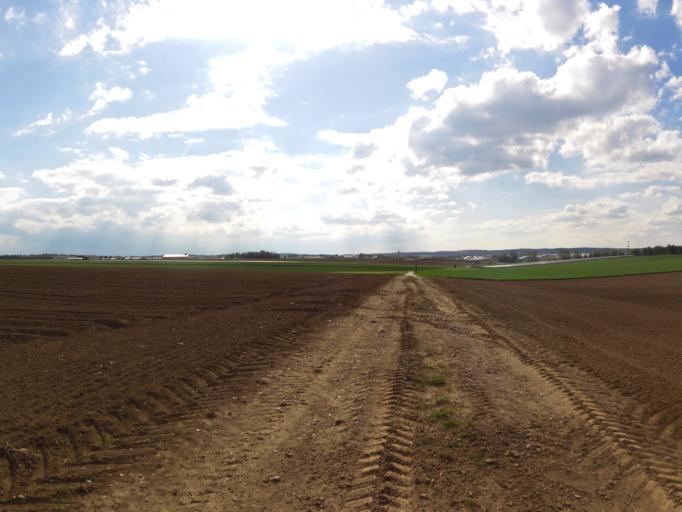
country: DE
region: Bavaria
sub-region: Regierungsbezirk Unterfranken
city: Oberpleichfeld
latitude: 49.8668
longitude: 10.0718
